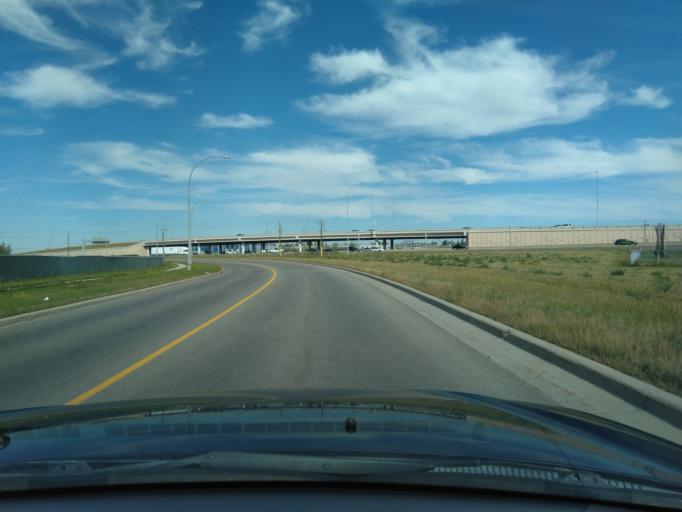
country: CA
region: Alberta
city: Calgary
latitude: 51.1009
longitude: -113.9841
